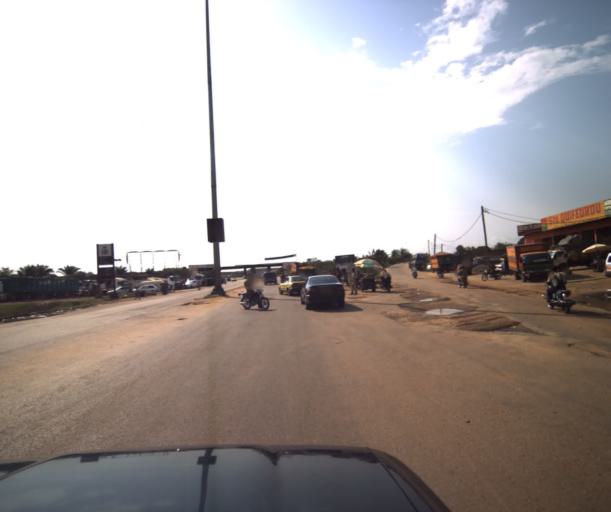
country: CM
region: Littoral
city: Douala
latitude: 4.0195
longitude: 9.7225
